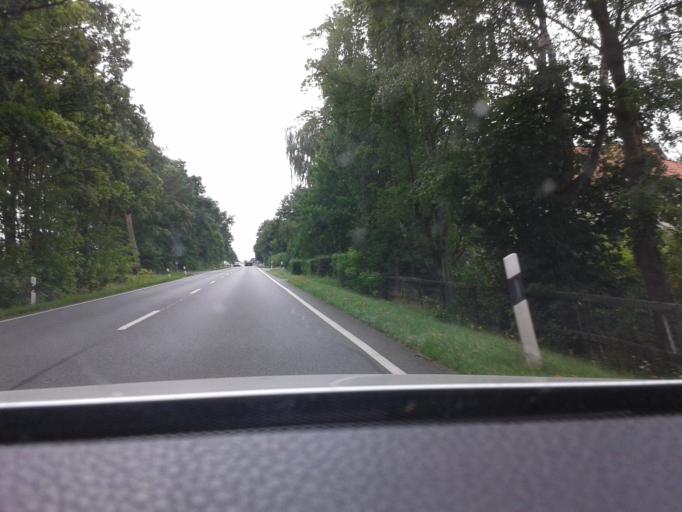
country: DE
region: Lower Saxony
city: Uetze
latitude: 52.4631
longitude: 10.1474
